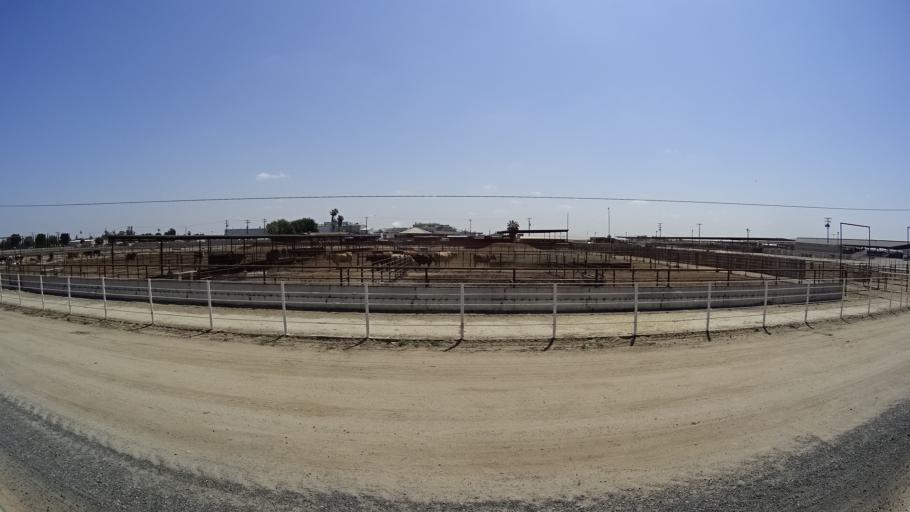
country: US
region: California
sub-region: Kings County
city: Home Garden
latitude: 36.3211
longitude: -119.6191
